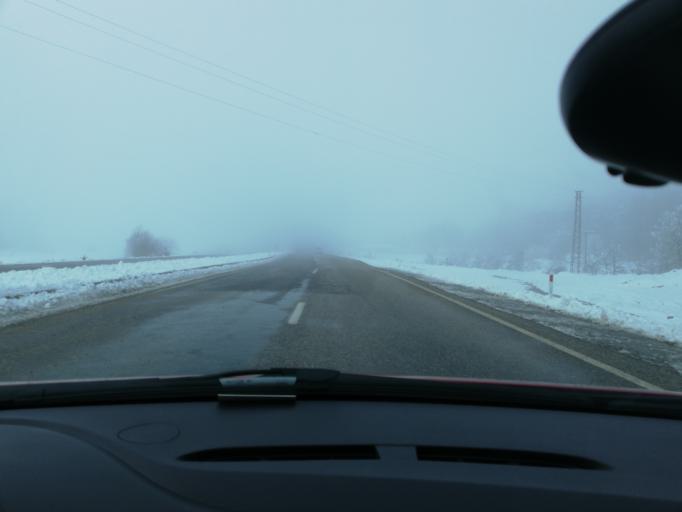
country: TR
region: Kastamonu
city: Akkaya
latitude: 41.2990
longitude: 33.5235
